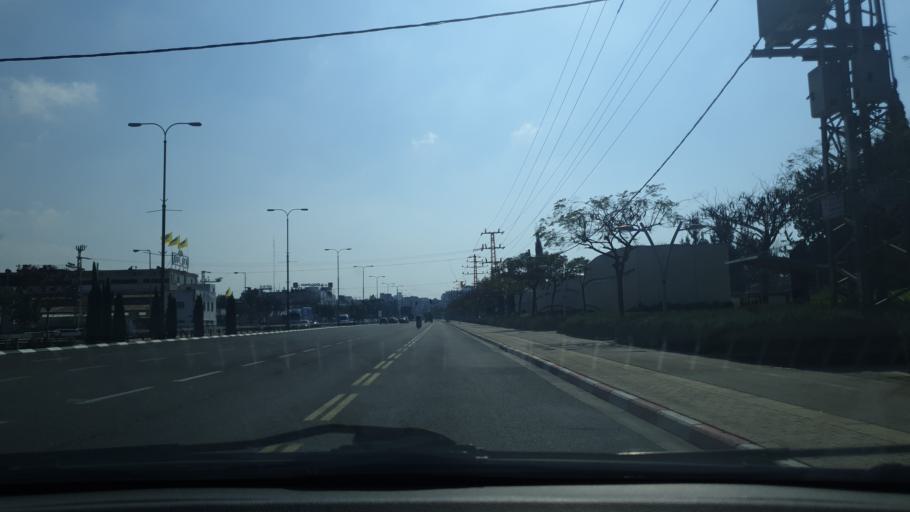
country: IL
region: Central District
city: Rishon LeZiyyon
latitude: 31.9787
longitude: 34.8084
